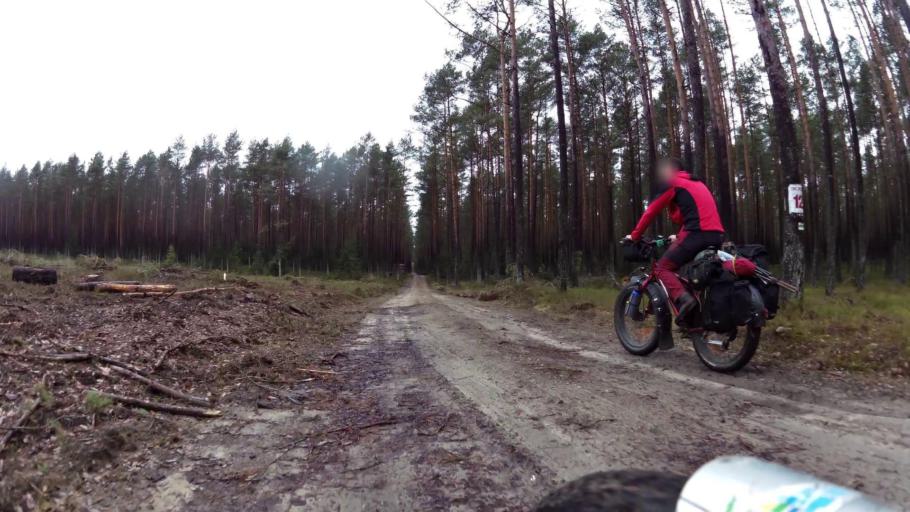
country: PL
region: Pomeranian Voivodeship
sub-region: Powiat bytowski
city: Borzytuchom
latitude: 54.2636
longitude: 17.3935
